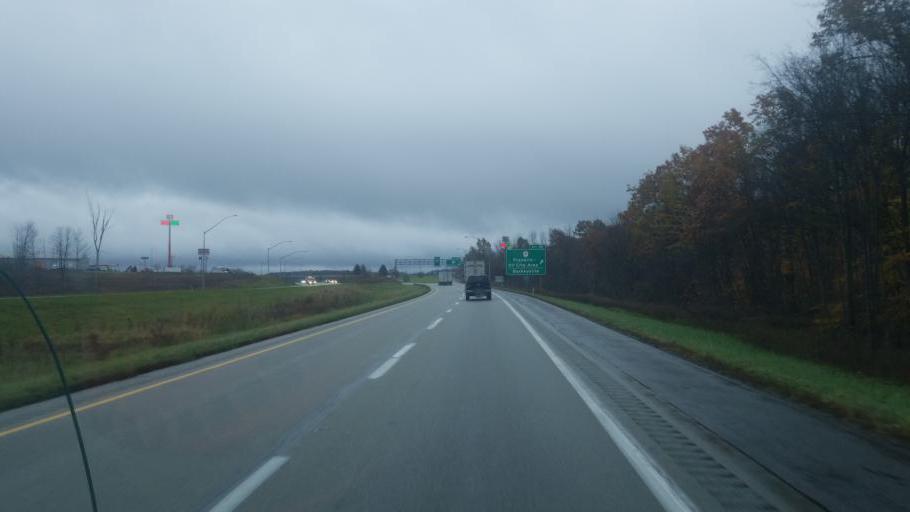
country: US
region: Pennsylvania
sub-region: Mercer County
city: Grove City
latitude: 41.2019
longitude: -79.9824
